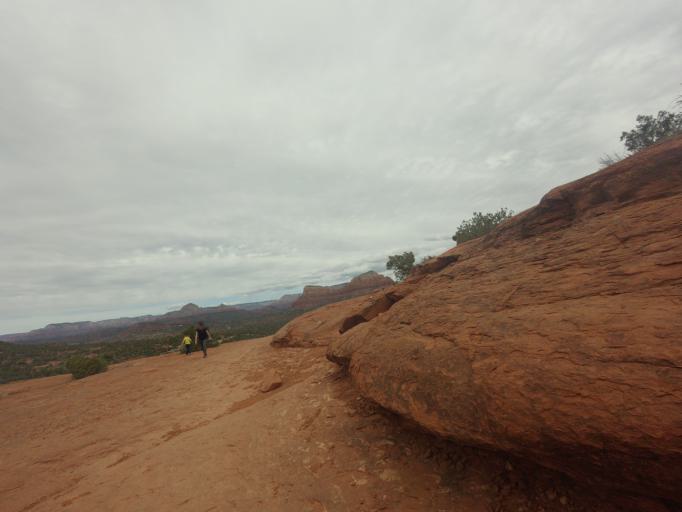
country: US
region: Arizona
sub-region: Yavapai County
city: Village of Oak Creek (Big Park)
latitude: 34.8016
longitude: -111.7660
